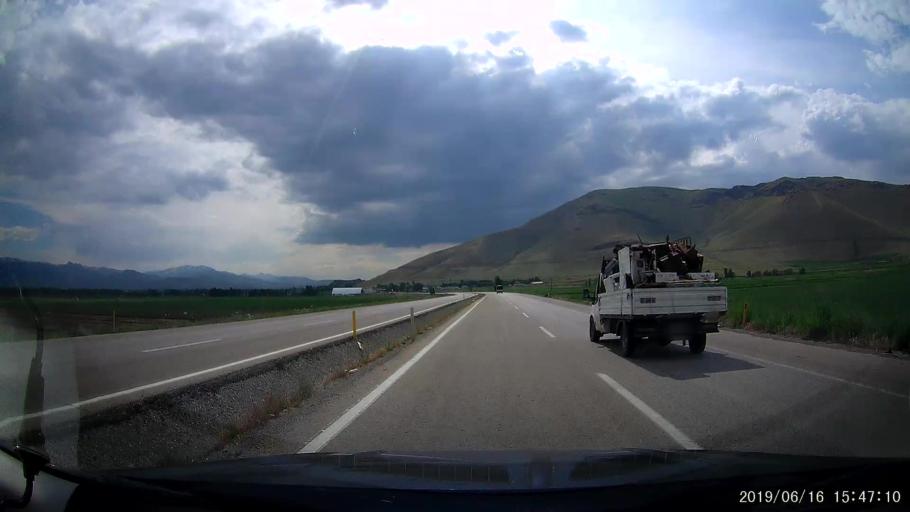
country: TR
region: Erzurum
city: Pasinler
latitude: 39.9889
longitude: 41.7271
